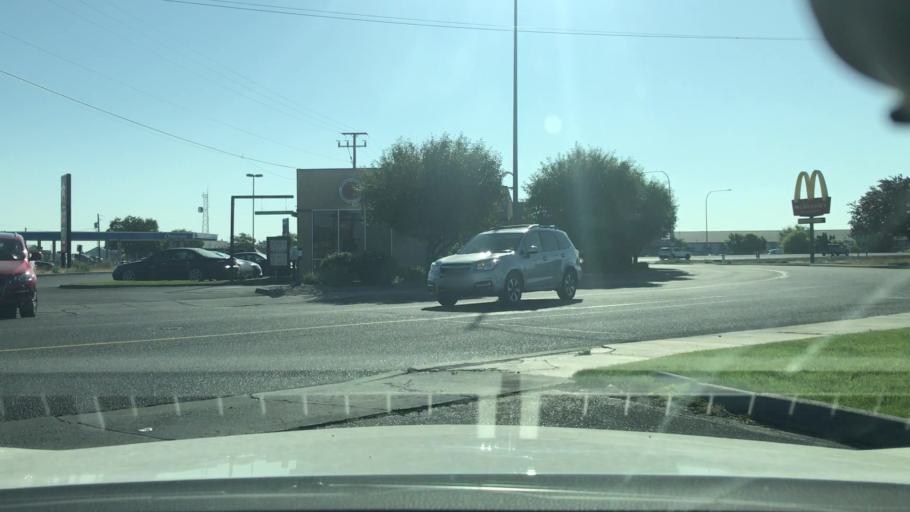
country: US
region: Washington
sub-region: Grant County
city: Moses Lake
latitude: 47.1015
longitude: -119.2480
